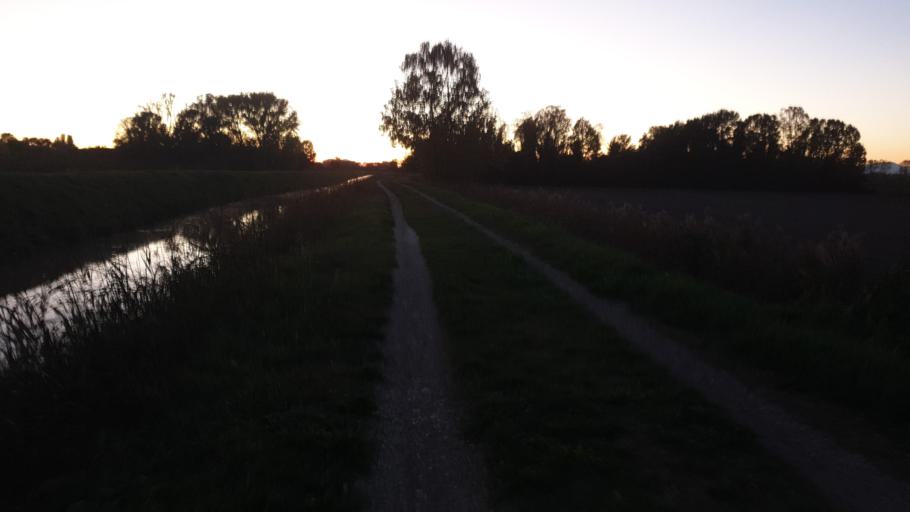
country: IT
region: Veneto
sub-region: Provincia di Venezia
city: Fiesso d'Artico
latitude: 45.4286
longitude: 12.0345
